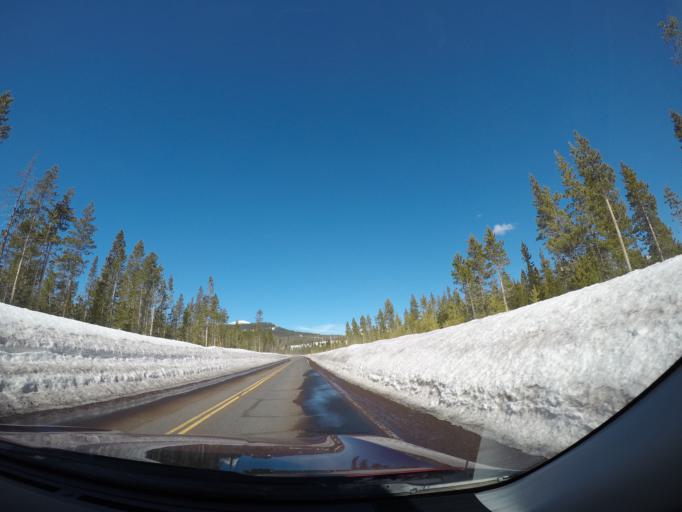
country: US
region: Oregon
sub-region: Deschutes County
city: Sunriver
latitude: 43.9777
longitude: -121.6109
